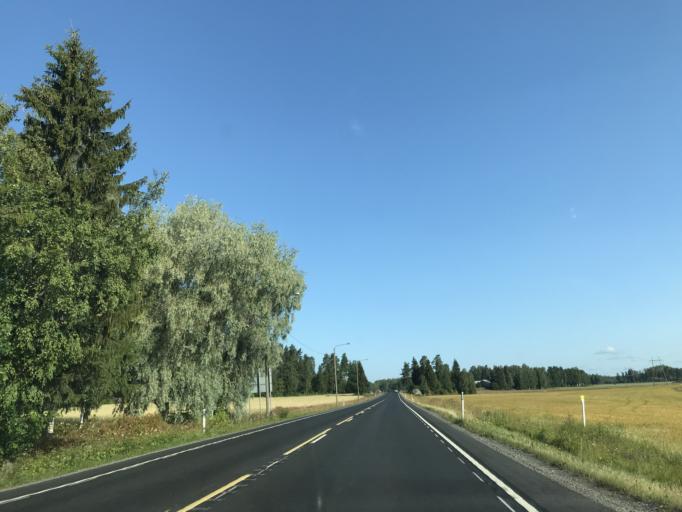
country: FI
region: Paijanne Tavastia
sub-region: Lahti
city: Lahti
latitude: 61.0946
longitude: 25.6464
